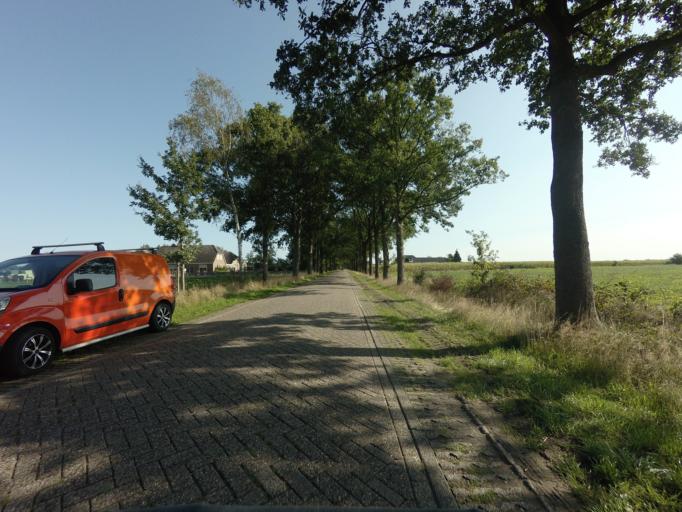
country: NL
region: Overijssel
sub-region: Gemeente Raalte
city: Raalte
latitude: 52.4193
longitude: 6.2889
